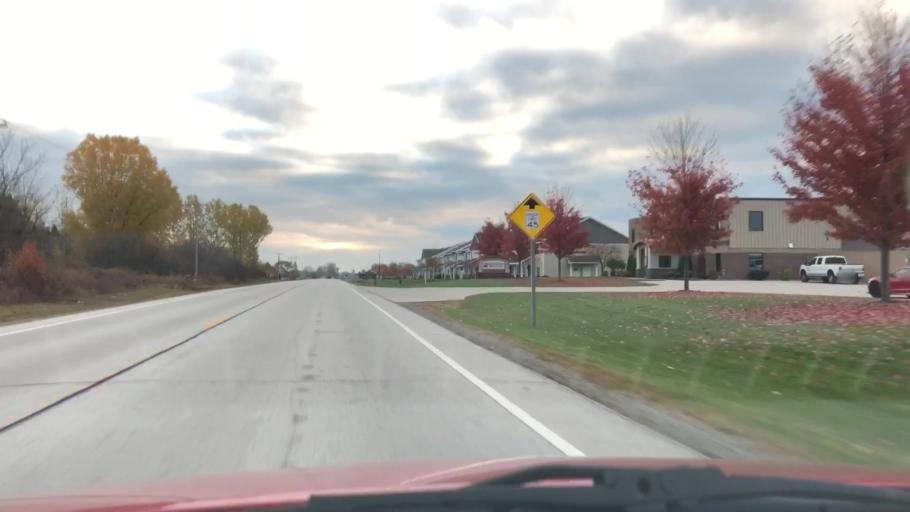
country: US
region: Wisconsin
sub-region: Brown County
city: Oneida
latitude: 44.4448
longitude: -88.1420
